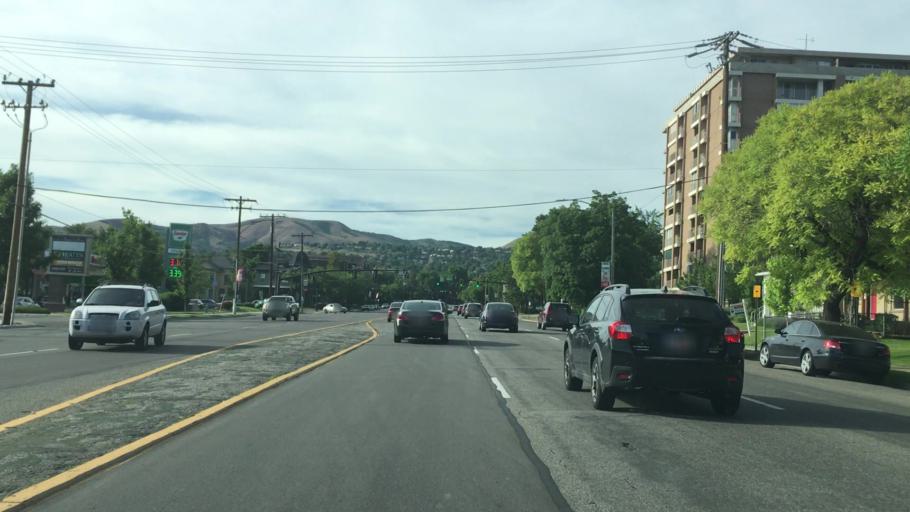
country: US
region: Utah
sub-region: Salt Lake County
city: Salt Lake City
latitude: 40.7637
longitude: -111.8710
